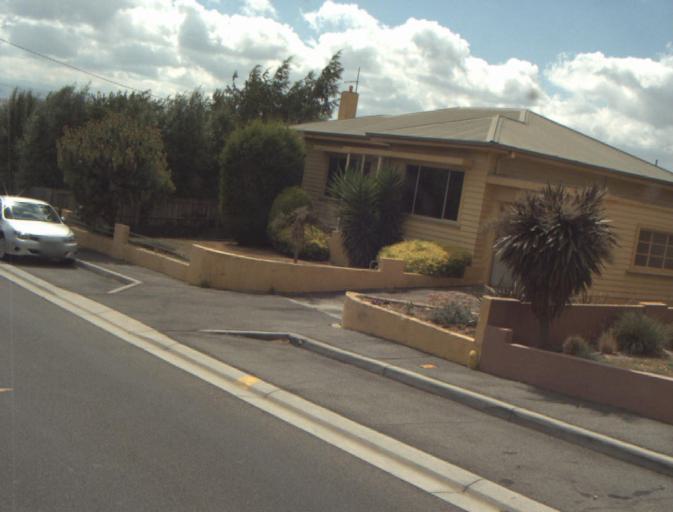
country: AU
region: Tasmania
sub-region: Launceston
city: Summerhill
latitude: -41.4664
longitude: 147.1560
